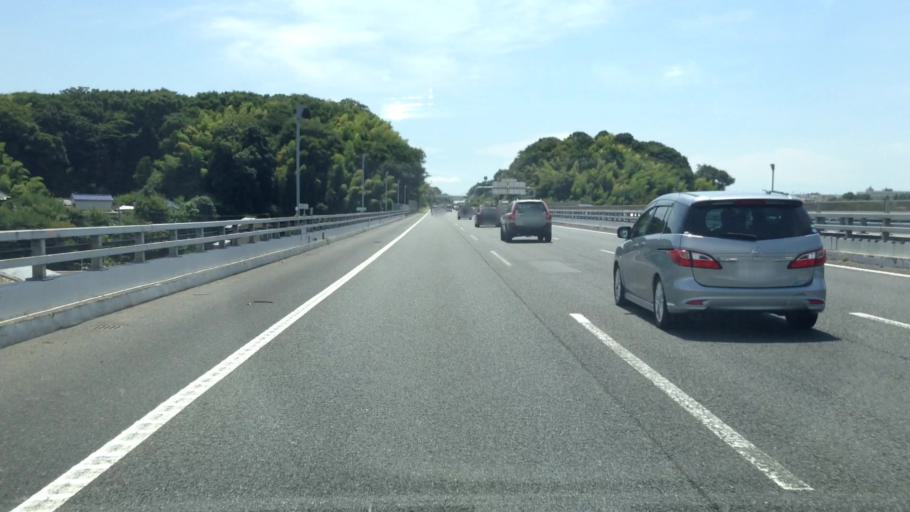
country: JP
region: Kanagawa
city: Yokohama
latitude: 35.5157
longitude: 139.5935
